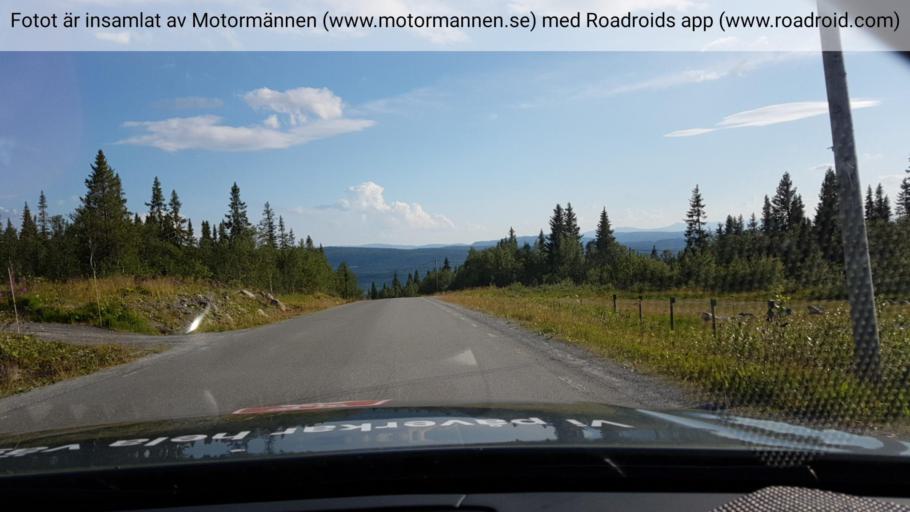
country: SE
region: Jaemtland
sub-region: Are Kommun
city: Are
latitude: 63.4226
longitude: 13.0185
